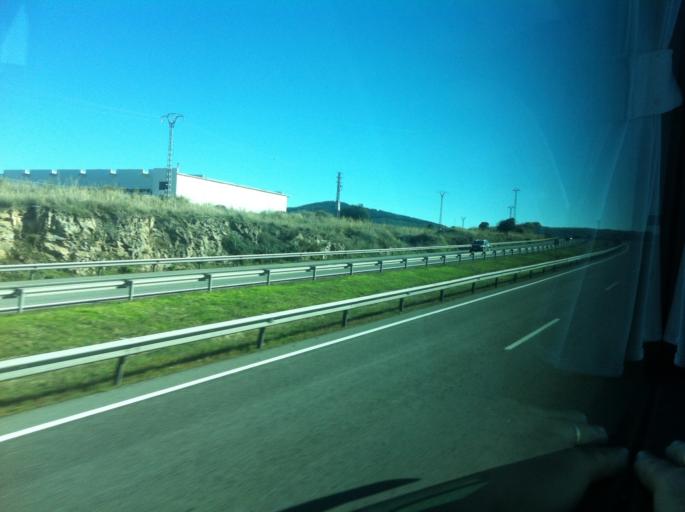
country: ES
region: Madrid
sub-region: Provincia de Madrid
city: Buitrago del Lozoya
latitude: 40.9911
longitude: -3.6423
